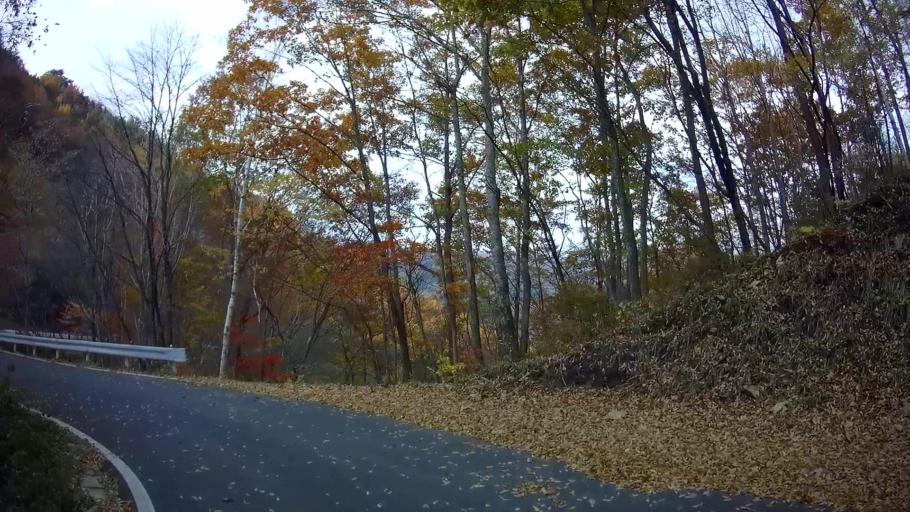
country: JP
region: Gunma
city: Nakanojomachi
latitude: 36.6334
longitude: 138.6486
